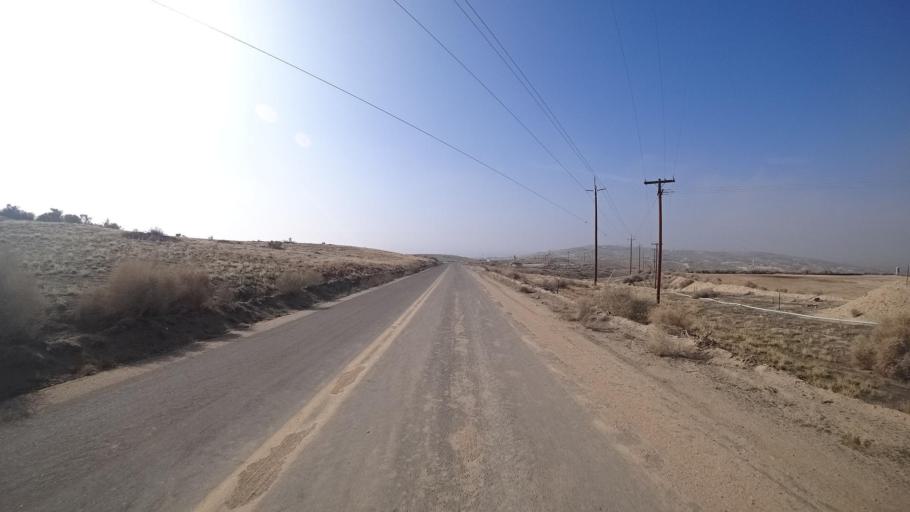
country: US
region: California
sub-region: Kern County
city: Ford City
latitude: 35.1649
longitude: -119.4145
